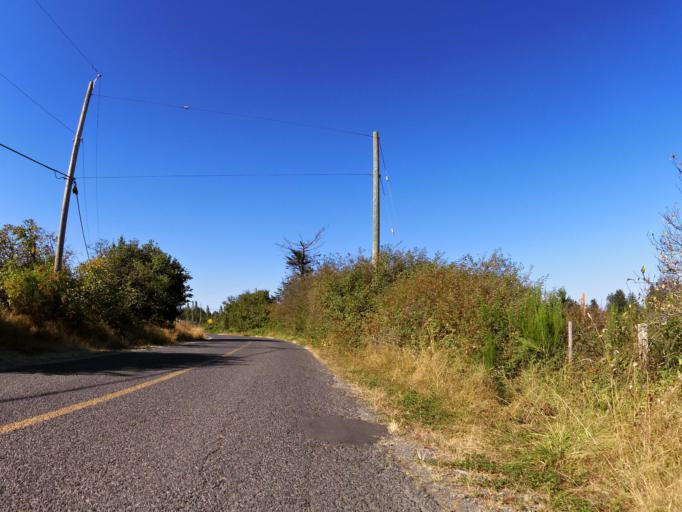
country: CA
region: British Columbia
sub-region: Cowichan Valley Regional District
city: Ladysmith
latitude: 49.0857
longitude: -123.8445
